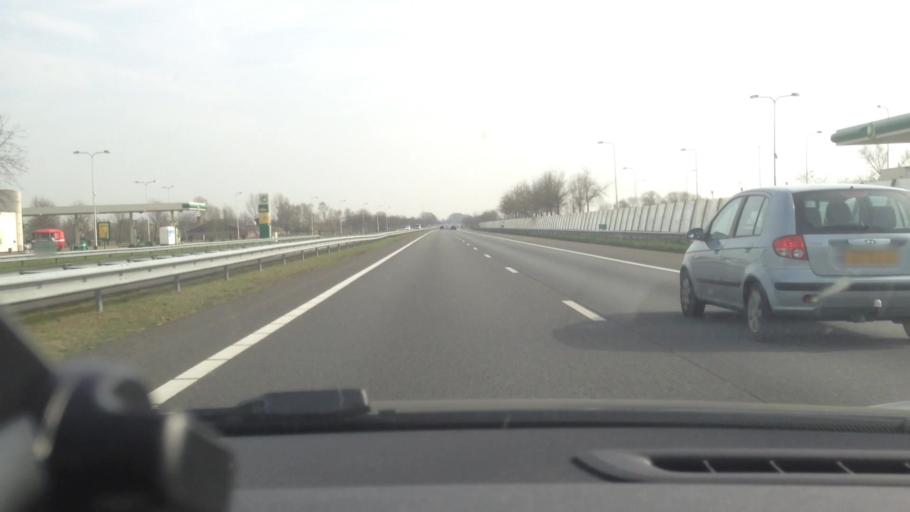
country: NL
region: Gelderland
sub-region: Gemeente Ede
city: Lunteren
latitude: 52.0646
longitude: 5.6098
